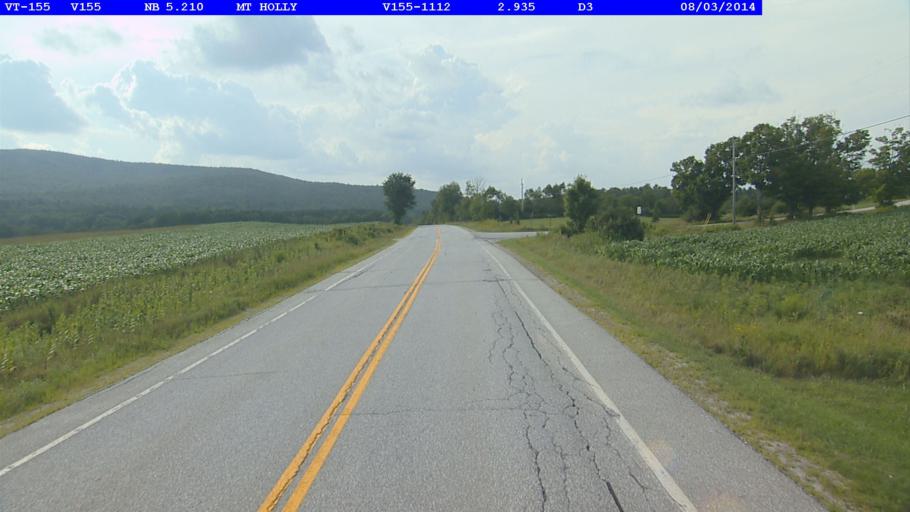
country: US
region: Vermont
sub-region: Windsor County
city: Chester
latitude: 43.3951
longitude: -72.8222
